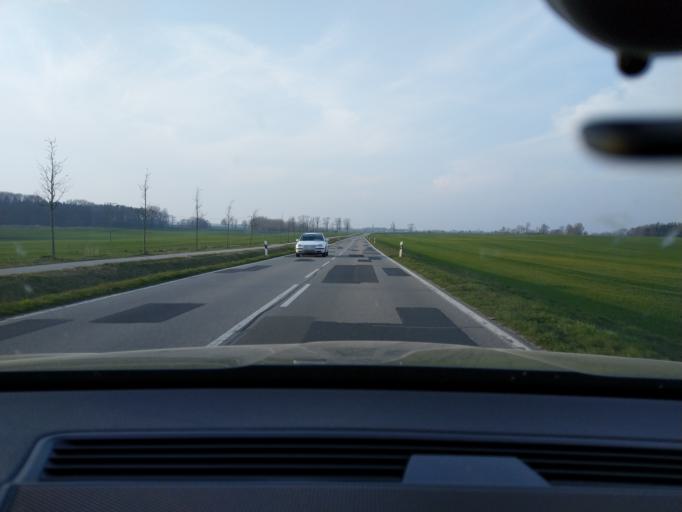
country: DE
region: Mecklenburg-Vorpommern
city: Kramerhof
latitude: 54.3427
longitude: 13.0305
